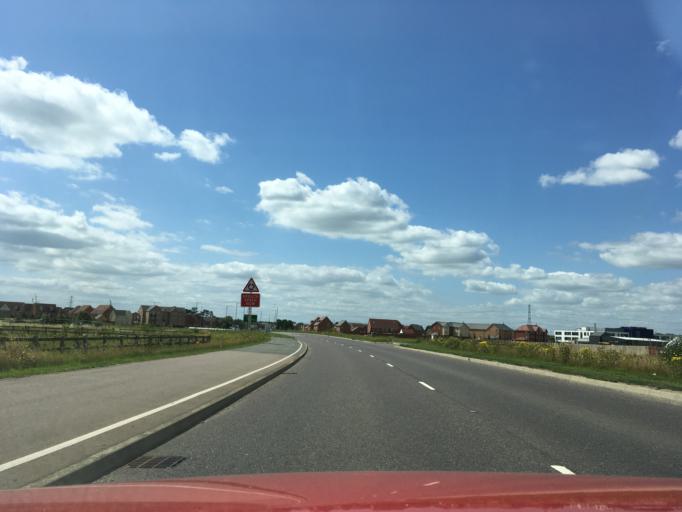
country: GB
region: England
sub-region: Buckinghamshire
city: Aylesbury
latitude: 51.8372
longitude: -0.8473
